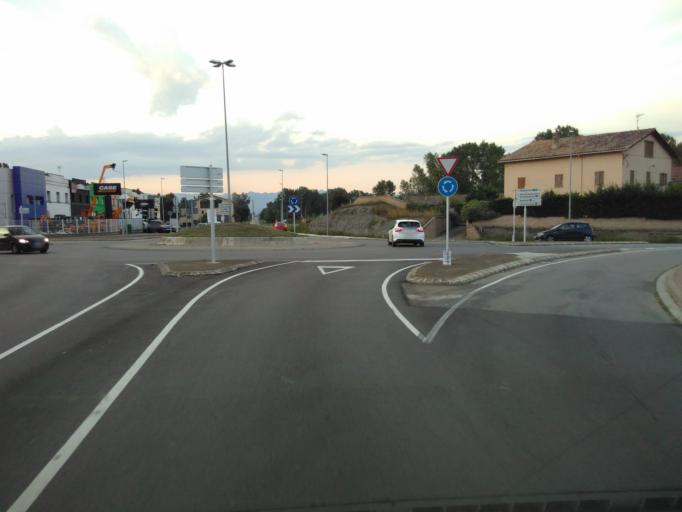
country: ES
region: Catalonia
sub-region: Provincia de Barcelona
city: Vic
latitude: 41.9460
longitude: 2.2588
